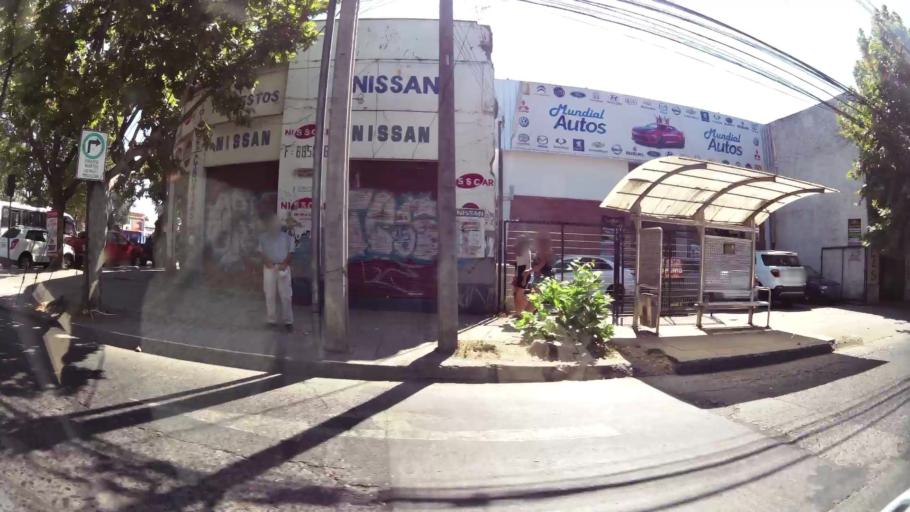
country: CL
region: Maule
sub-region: Provincia de Talca
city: Talca
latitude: -35.4292
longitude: -71.6505
